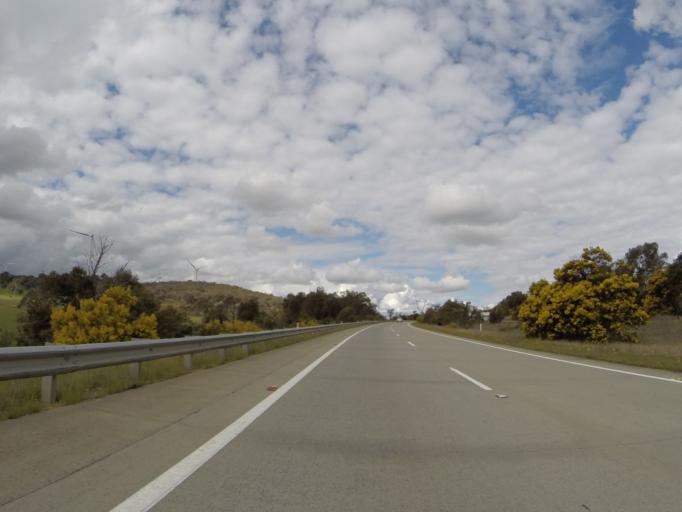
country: AU
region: New South Wales
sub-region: Yass Valley
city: Gundaroo
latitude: -34.8198
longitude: 149.3861
